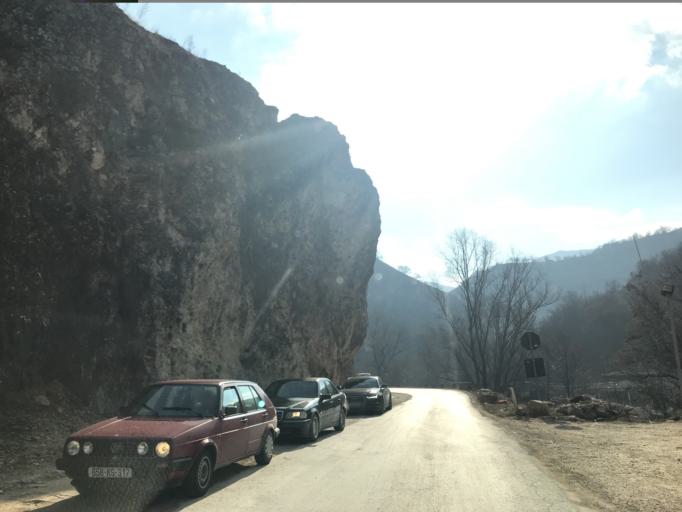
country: XK
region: Prizren
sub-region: Prizren
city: Prizren
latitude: 42.2095
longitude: 20.7503
